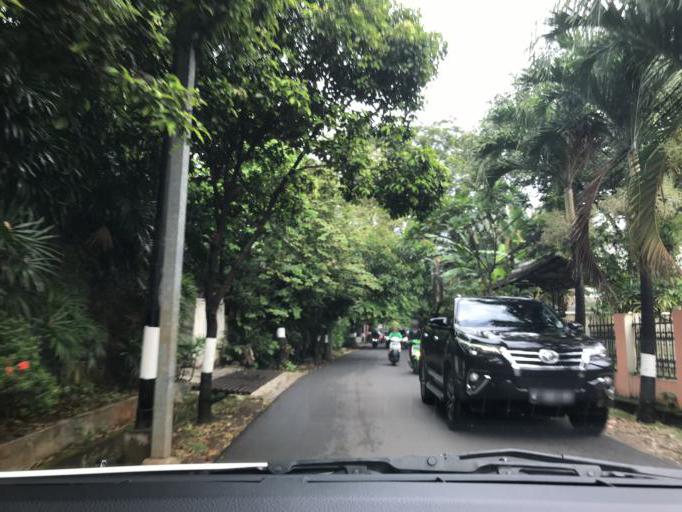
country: ID
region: Jakarta Raya
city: Jakarta
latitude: -6.2874
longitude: 106.8054
